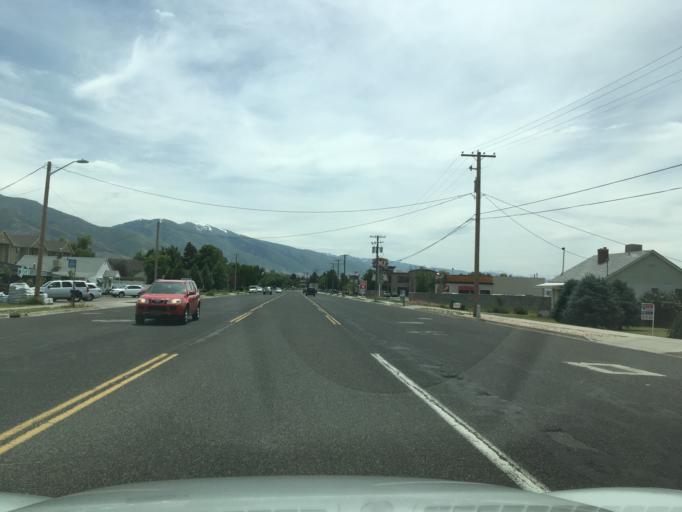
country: US
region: Utah
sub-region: Davis County
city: Layton
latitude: 41.0490
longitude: -111.9566
